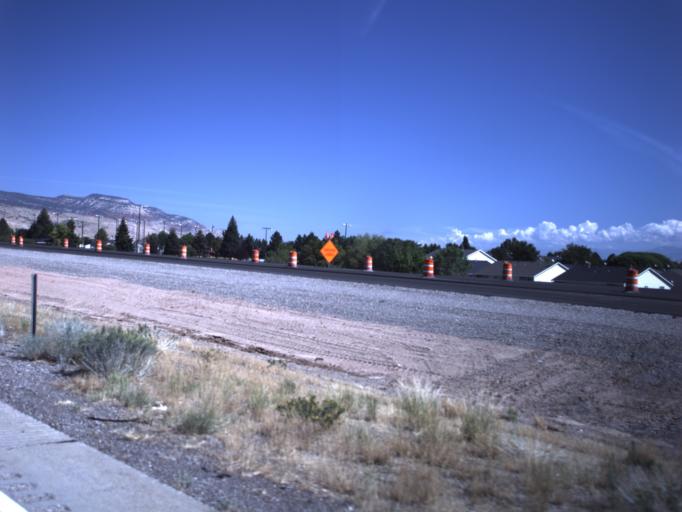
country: US
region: Utah
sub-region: Sevier County
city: Richfield
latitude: 38.7550
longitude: -112.1053
